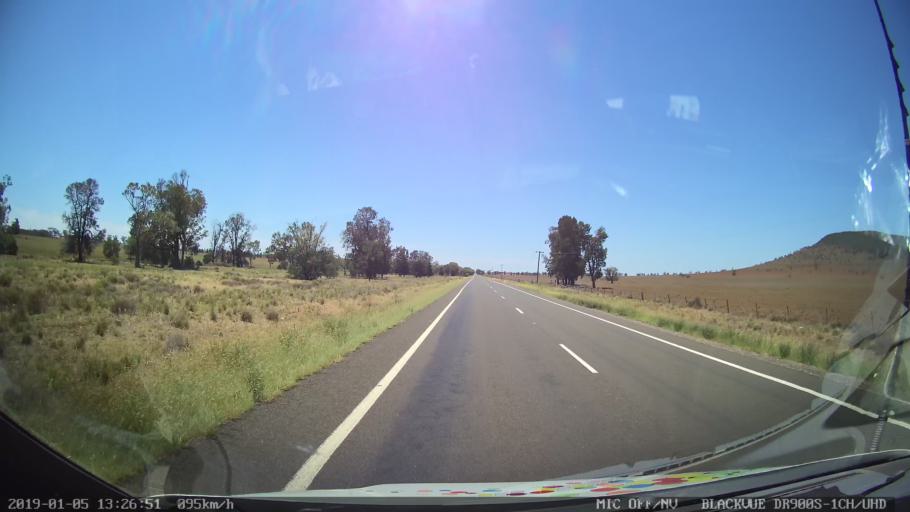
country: AU
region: New South Wales
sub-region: Gunnedah
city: Gunnedah
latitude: -31.0495
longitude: 150.0213
